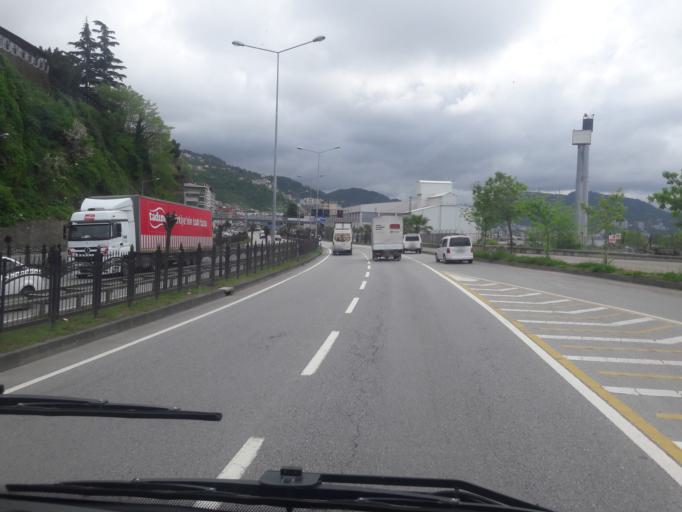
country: TR
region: Giresun
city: Giresun
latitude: 40.9234
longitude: 38.3896
